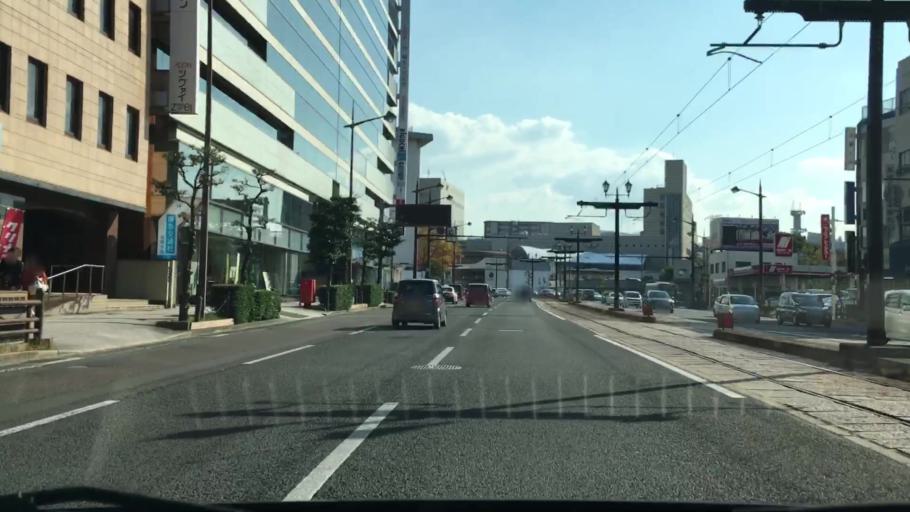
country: JP
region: Nagasaki
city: Nagasaki-shi
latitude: 32.7551
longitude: 129.8704
